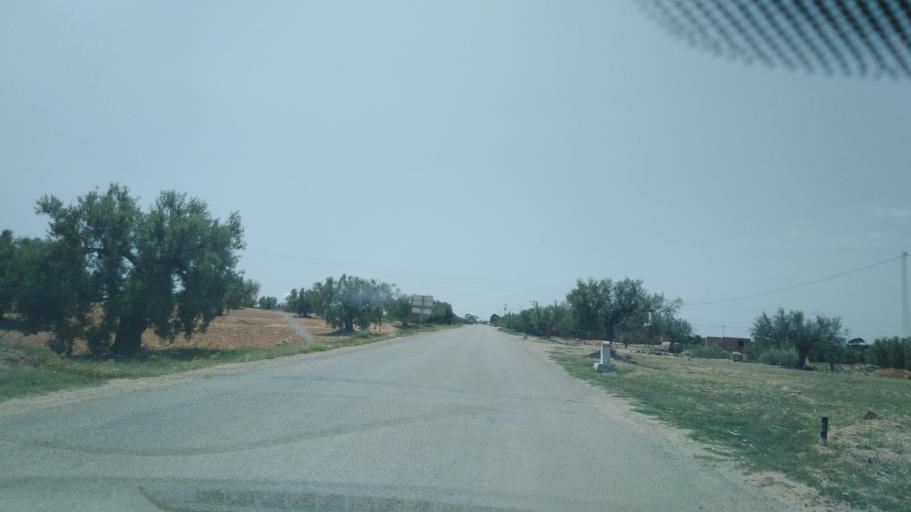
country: TN
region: Safaqis
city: Sfax
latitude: 34.7298
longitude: 10.5772
